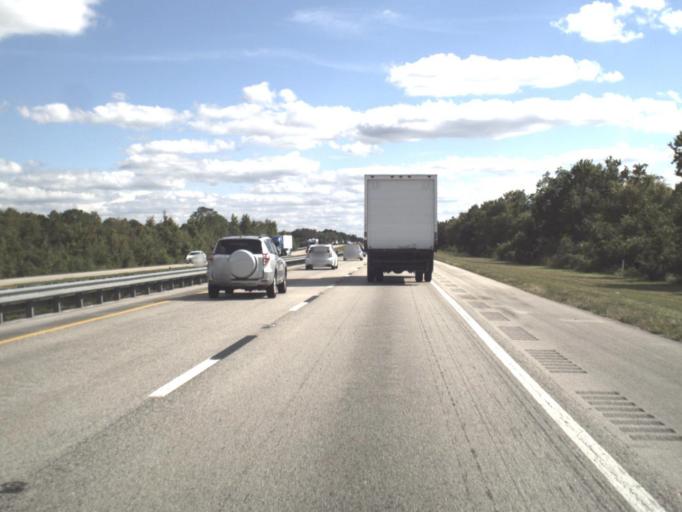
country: US
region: Florida
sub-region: Indian River County
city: Fellsmere
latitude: 27.6477
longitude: -80.8571
